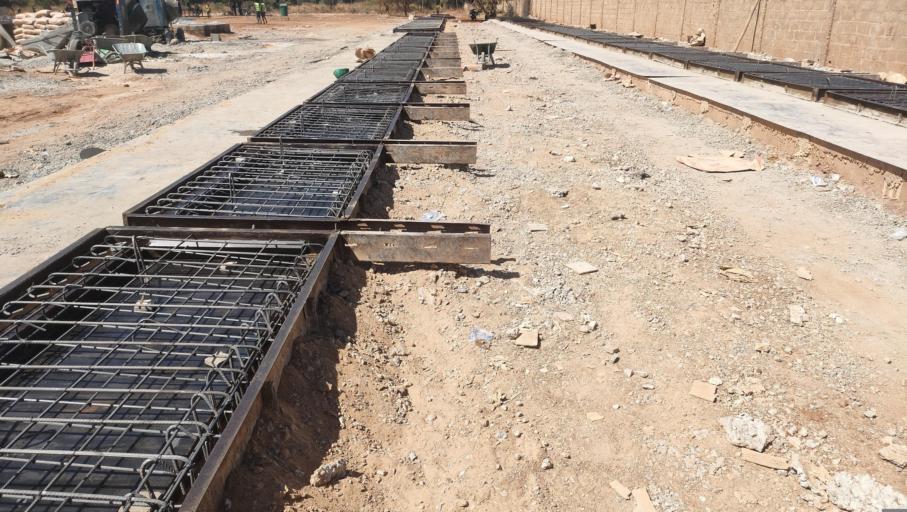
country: BF
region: Est
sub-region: Province du Gourma
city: Fada N'gourma
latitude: 12.0914
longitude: 0.3516
